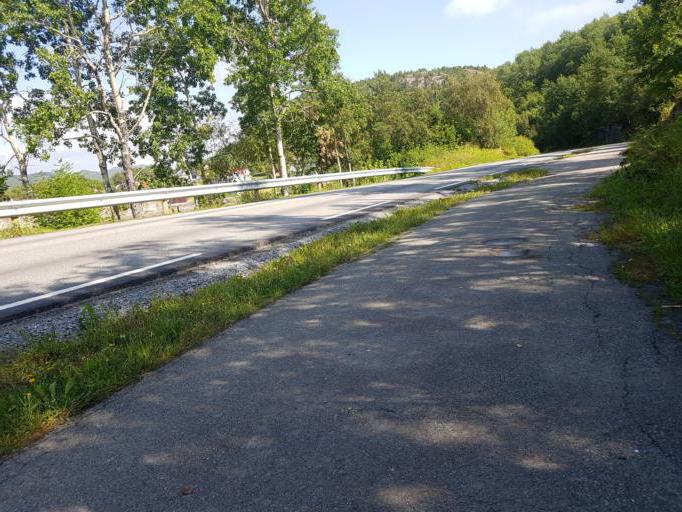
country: NO
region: Sor-Trondelag
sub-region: Agdenes
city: Lensvik
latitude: 63.6349
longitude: 9.8328
